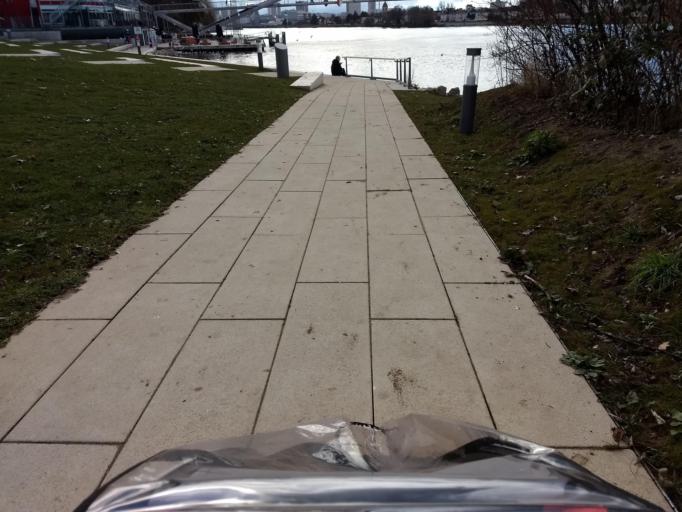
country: FR
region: Alsace
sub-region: Departement du Haut-Rhin
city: Huningue
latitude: 47.5926
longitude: 7.5921
